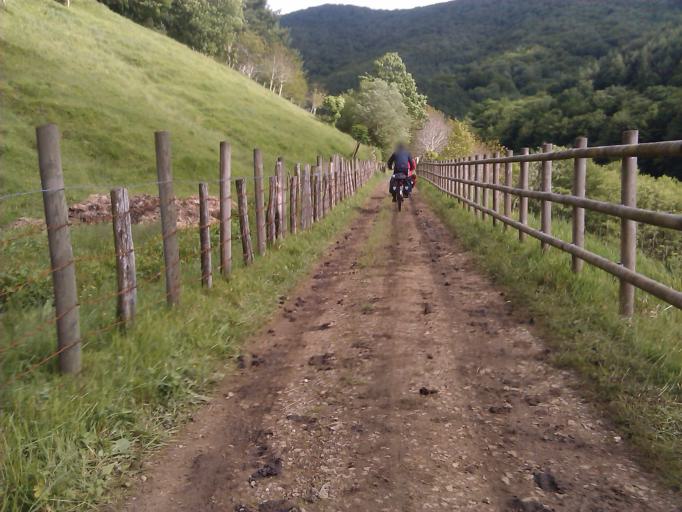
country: ES
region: Navarre
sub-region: Provincia de Navarra
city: Leitza
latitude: 43.0580
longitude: -1.9017
